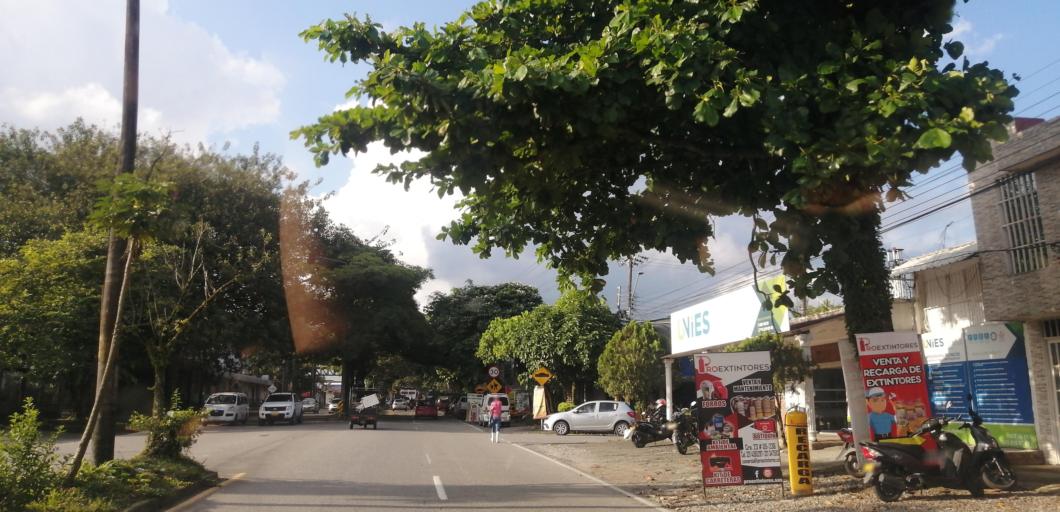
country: CO
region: Meta
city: Acacias
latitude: 3.9801
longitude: -73.7668
